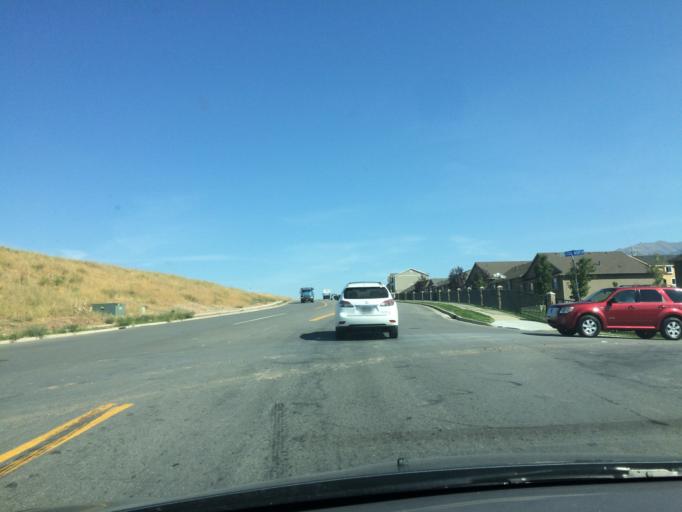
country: US
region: Utah
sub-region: Davis County
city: South Weber
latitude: 41.1029
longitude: -111.9331
